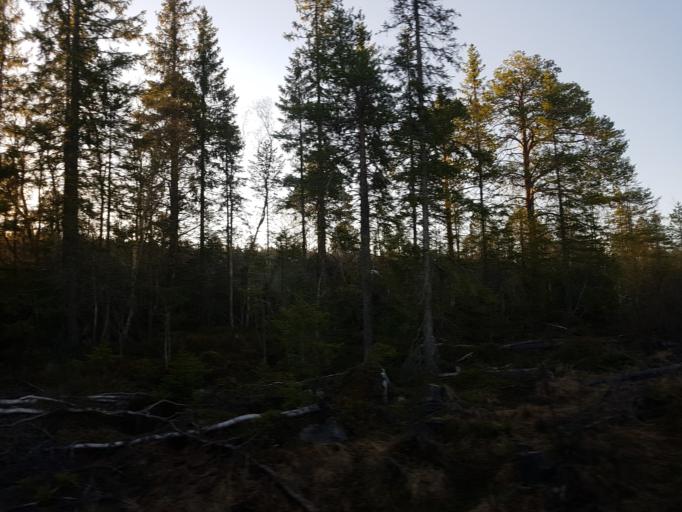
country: NO
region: Sor-Trondelag
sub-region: Rennebu
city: Berkak
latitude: 62.8334
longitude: 10.0217
